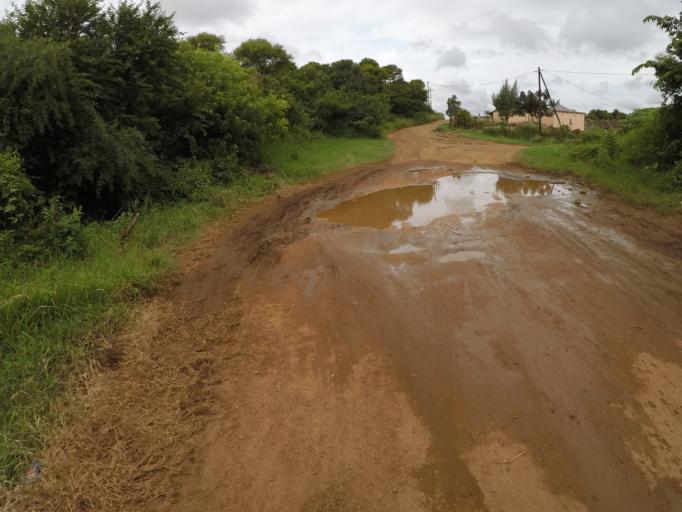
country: ZA
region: KwaZulu-Natal
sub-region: uThungulu District Municipality
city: Empangeni
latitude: -28.7787
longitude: 31.8693
